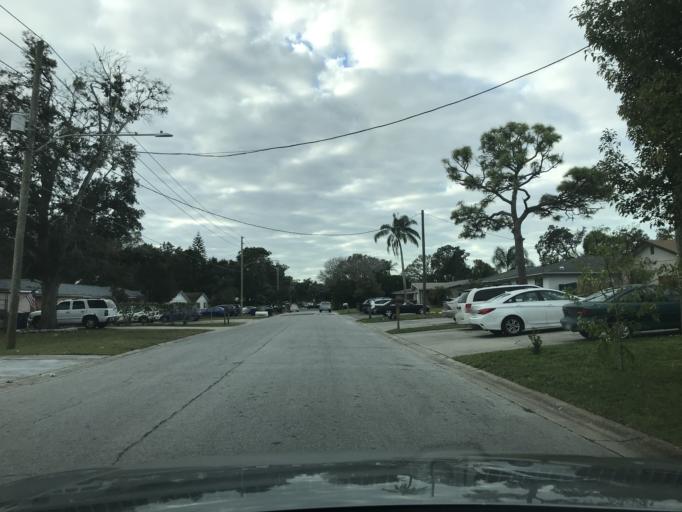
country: US
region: Florida
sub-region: Pinellas County
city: Clearwater
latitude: 27.9477
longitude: -82.7840
